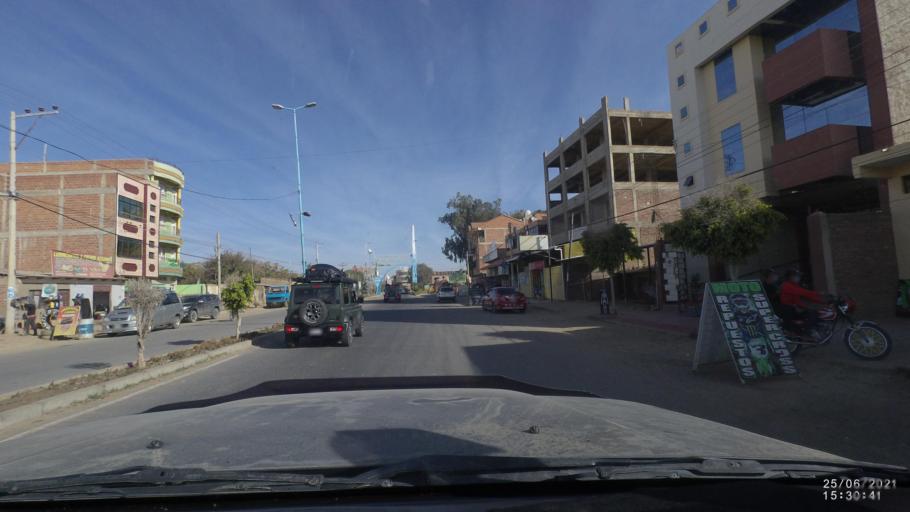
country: BO
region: Cochabamba
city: Cliza
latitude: -17.5870
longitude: -65.9339
